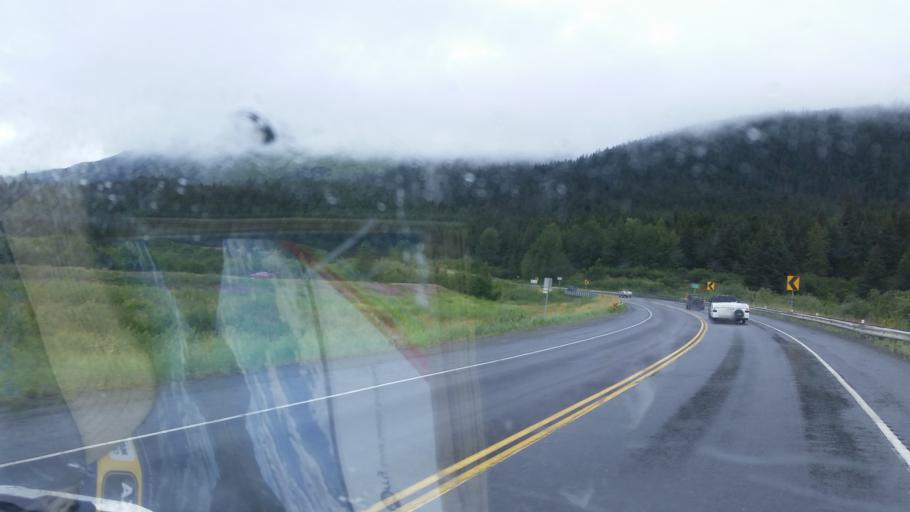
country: US
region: Alaska
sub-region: Anchorage Municipality
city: Girdwood
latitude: 60.8462
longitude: -149.0556
